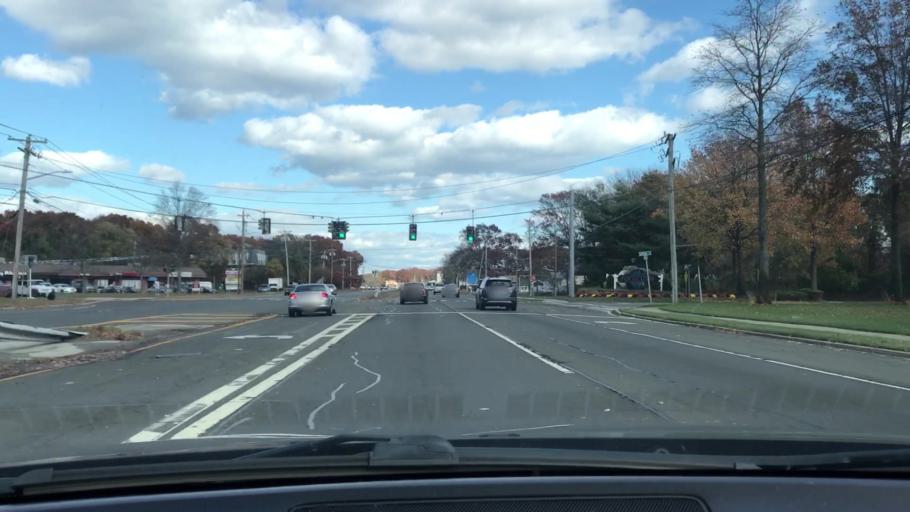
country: US
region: New York
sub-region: Suffolk County
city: Terryville
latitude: 40.9139
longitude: -73.0587
